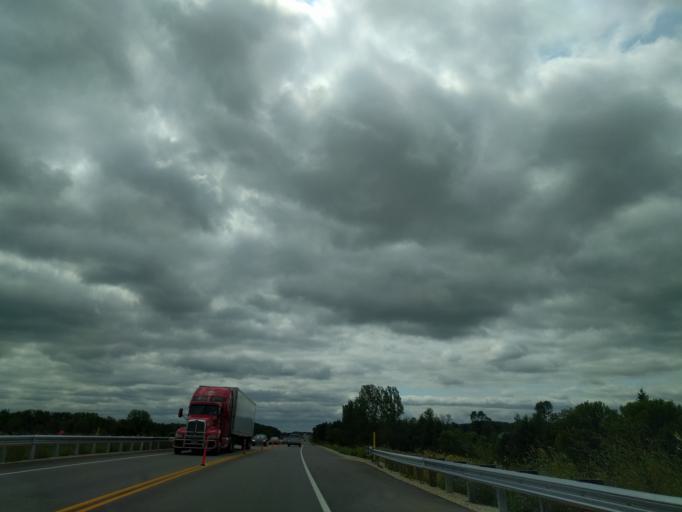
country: US
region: Wisconsin
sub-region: Manitowoc County
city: Manitowoc
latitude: 44.0229
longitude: -87.7090
